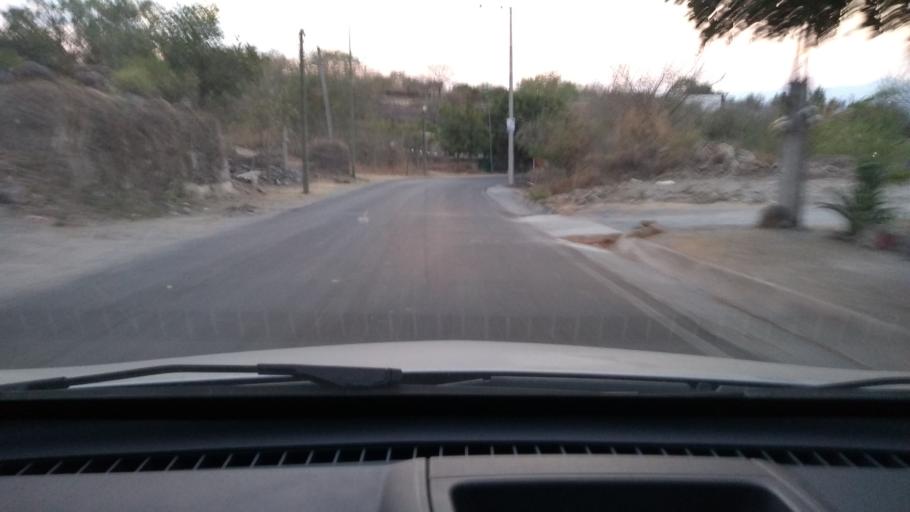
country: MX
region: Morelos
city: Coatetelco
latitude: 18.7232
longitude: -99.3151
